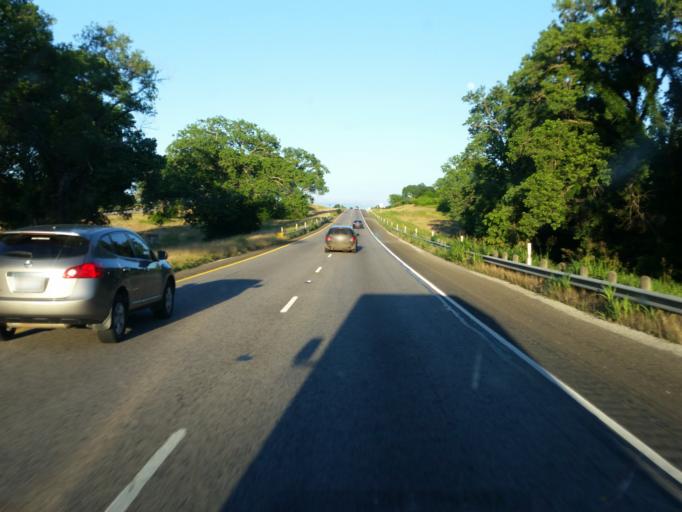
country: US
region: Texas
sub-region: Van Zandt County
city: Wills Point
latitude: 32.6657
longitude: -96.1353
